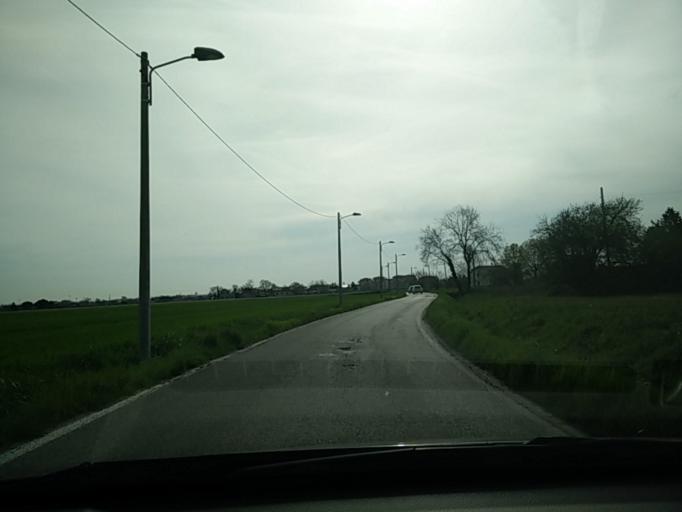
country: IT
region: Emilia-Romagna
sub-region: Provincia di Rimini
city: Santa Giustina
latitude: 44.0758
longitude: 12.5064
